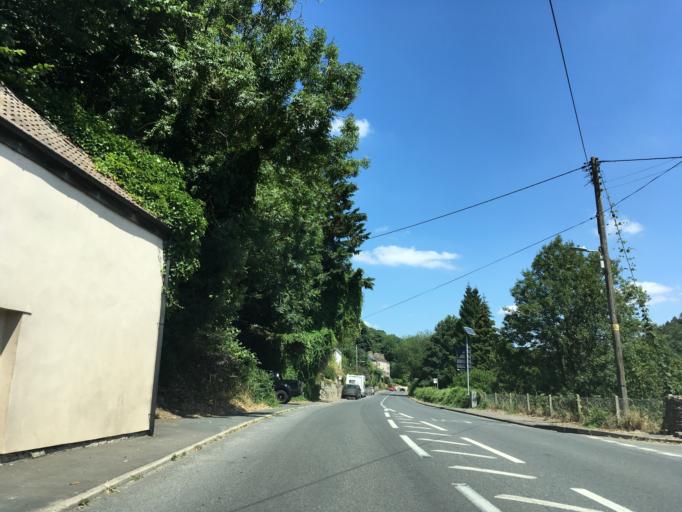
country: GB
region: England
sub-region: Gloucestershire
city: Chalford
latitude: 51.7191
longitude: -2.1656
